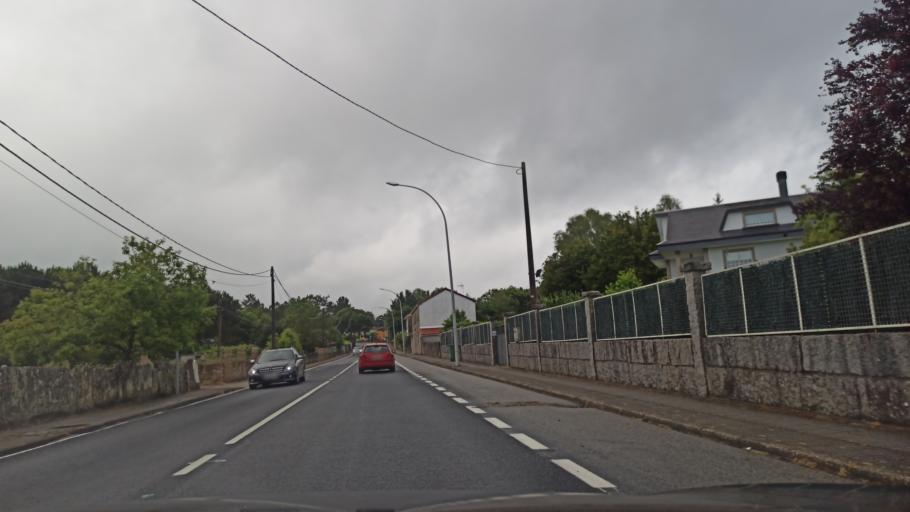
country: ES
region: Galicia
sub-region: Provincia da Coruna
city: Santiso
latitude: 42.7649
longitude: -8.0206
